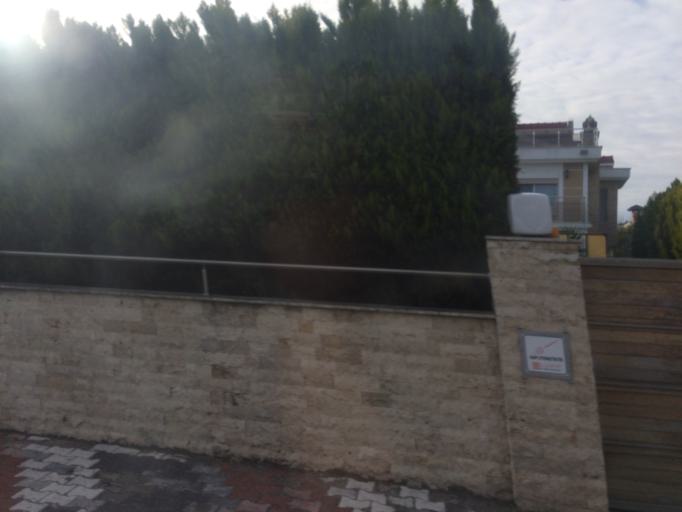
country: TR
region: Izmir
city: Menemen
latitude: 38.5022
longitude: 26.9595
